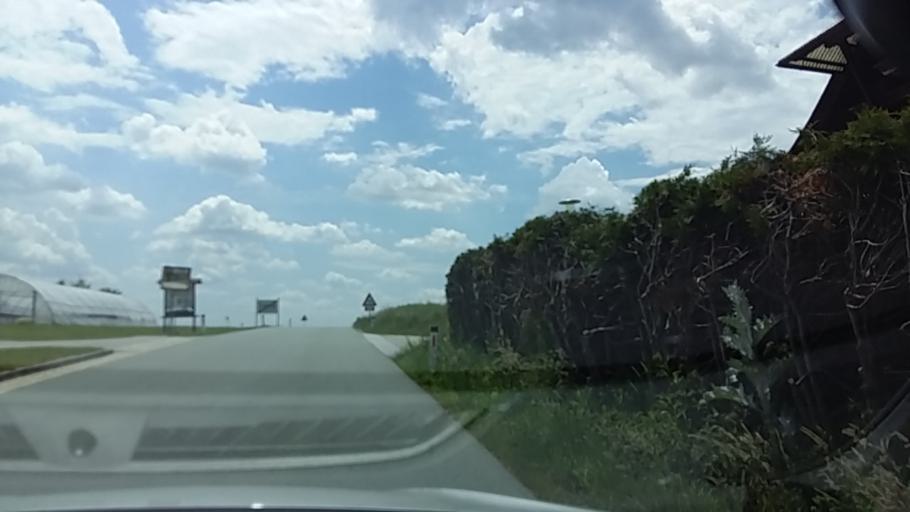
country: AT
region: Styria
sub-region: Politischer Bezirk Hartberg-Fuerstenfeld
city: Bad Blumau
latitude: 47.1166
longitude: 15.9993
